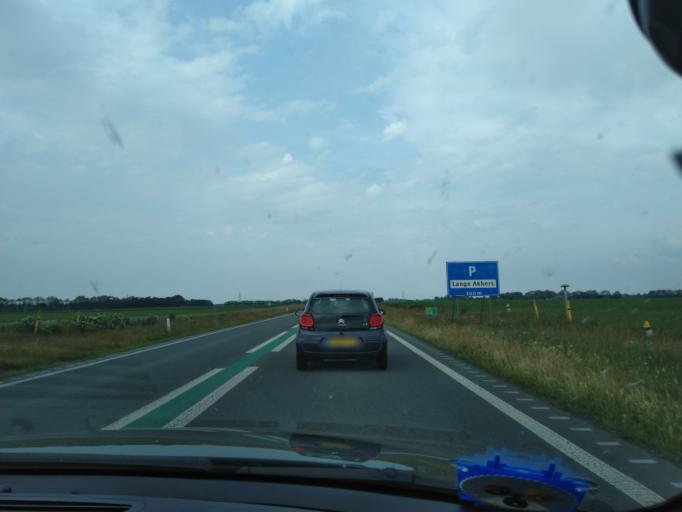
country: NL
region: Drenthe
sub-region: Gemeente Coevorden
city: Dalen
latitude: 52.7123
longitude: 6.7590
